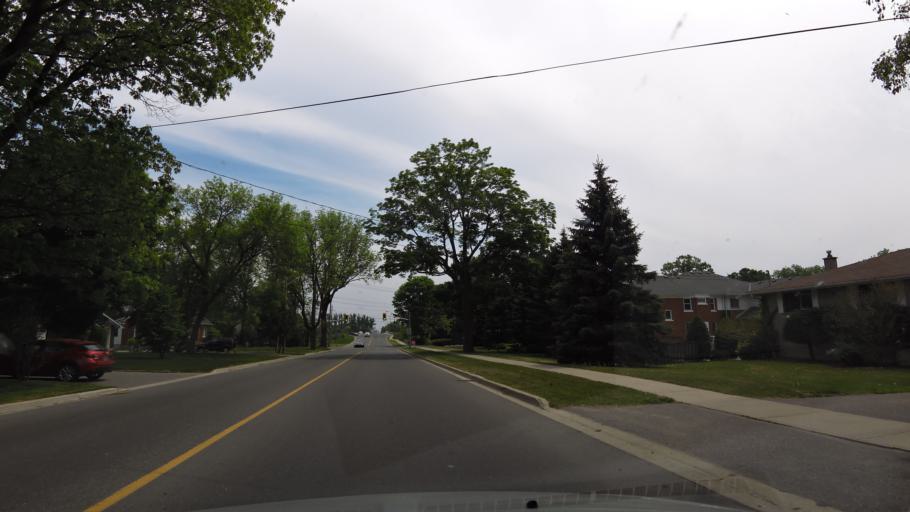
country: CA
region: Ontario
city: Oshawa
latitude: 43.9131
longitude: -78.5869
